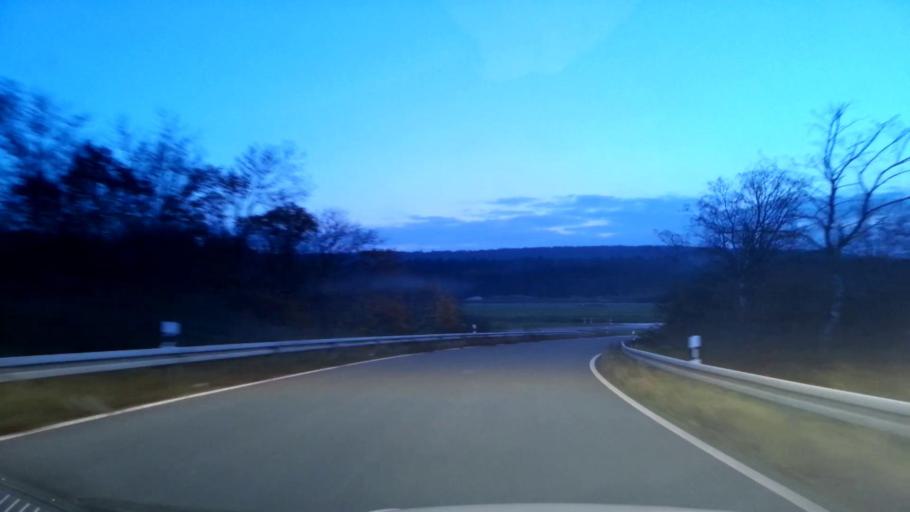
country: DE
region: Bavaria
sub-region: Upper Franconia
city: Pettstadt
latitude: 49.8309
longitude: 10.9498
